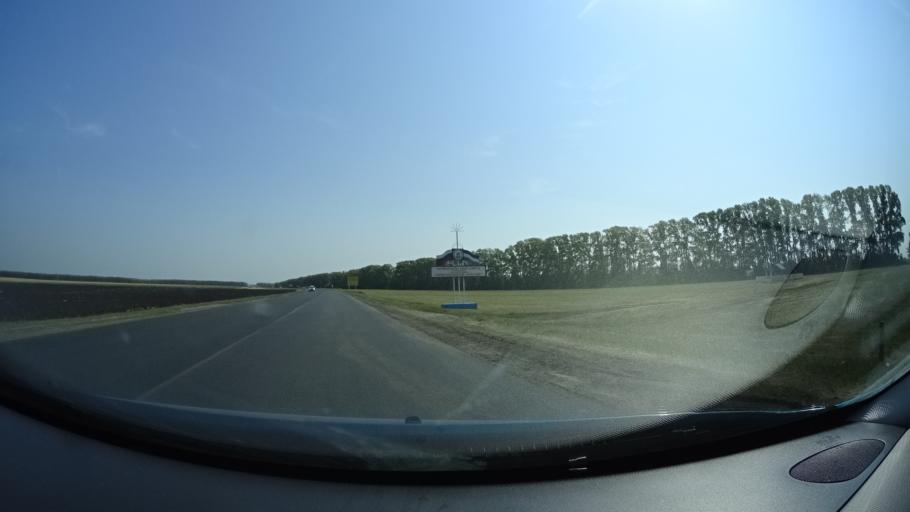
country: RU
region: Bashkortostan
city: Karmaskaly
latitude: 54.3853
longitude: 56.1425
